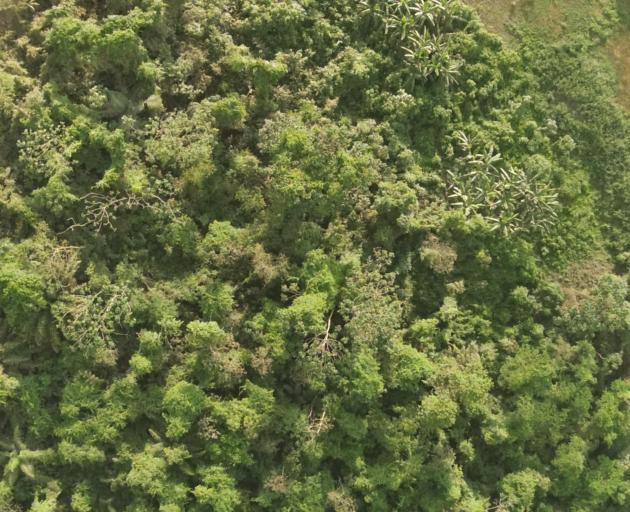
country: BO
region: La Paz
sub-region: Provincia Larecaja
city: Guanay
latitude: -15.7722
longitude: -67.6603
